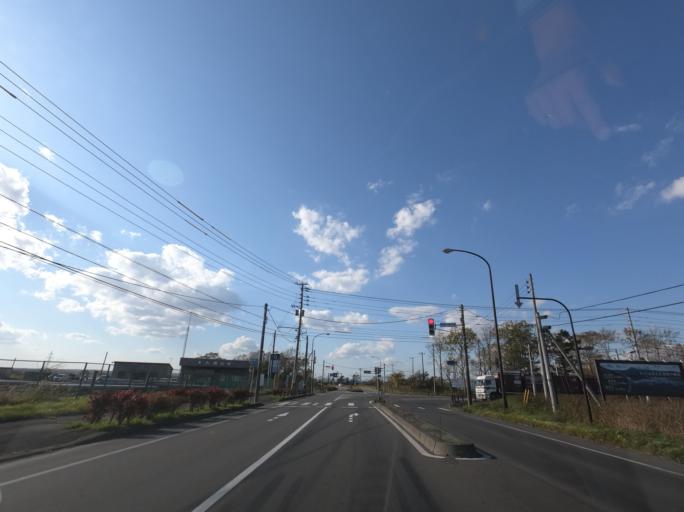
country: JP
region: Hokkaido
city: Kushiro
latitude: 43.0541
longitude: 144.2955
